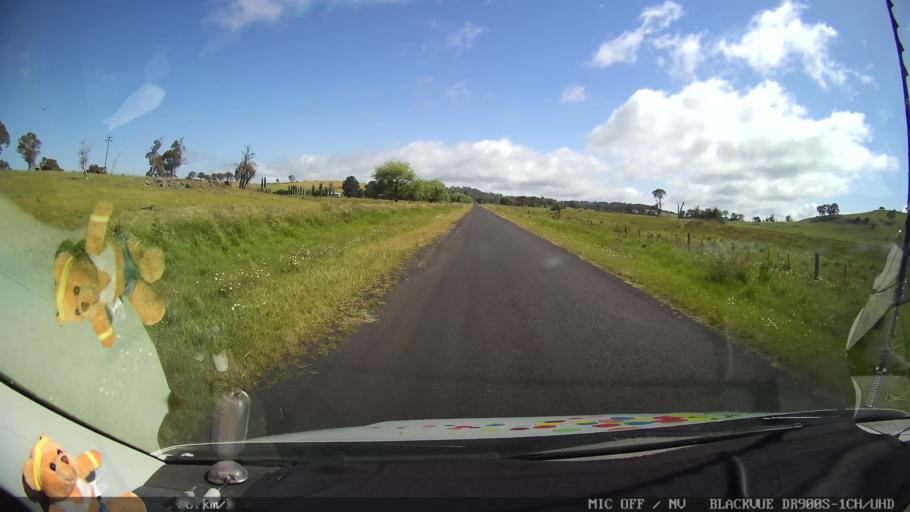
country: AU
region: New South Wales
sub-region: Guyra
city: Guyra
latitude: -30.0543
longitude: 151.6652
